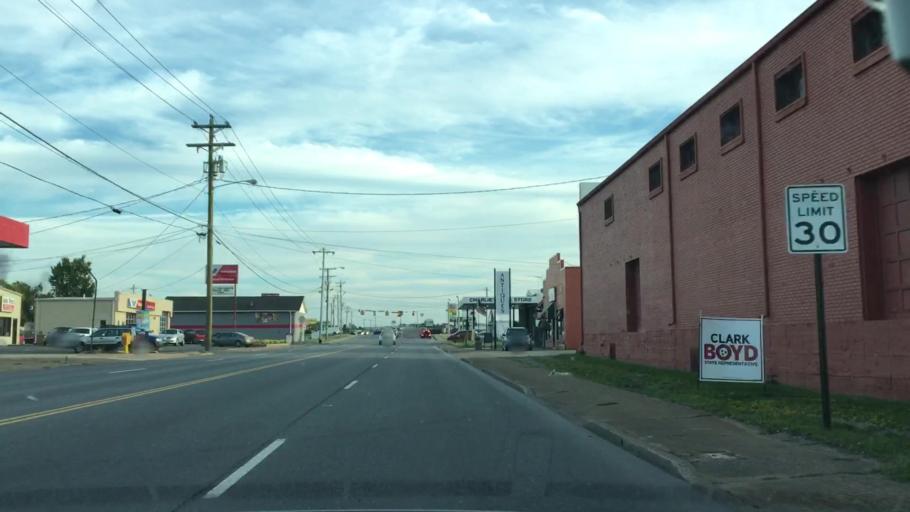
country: US
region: Tennessee
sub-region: Wilson County
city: Lebanon
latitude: 36.2024
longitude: -86.2920
